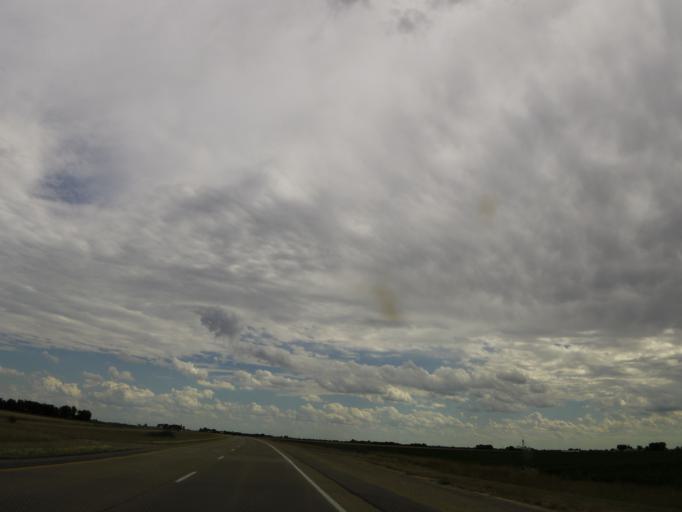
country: US
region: Iowa
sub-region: Henry County
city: Winfield
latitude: 41.0983
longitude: -91.5449
